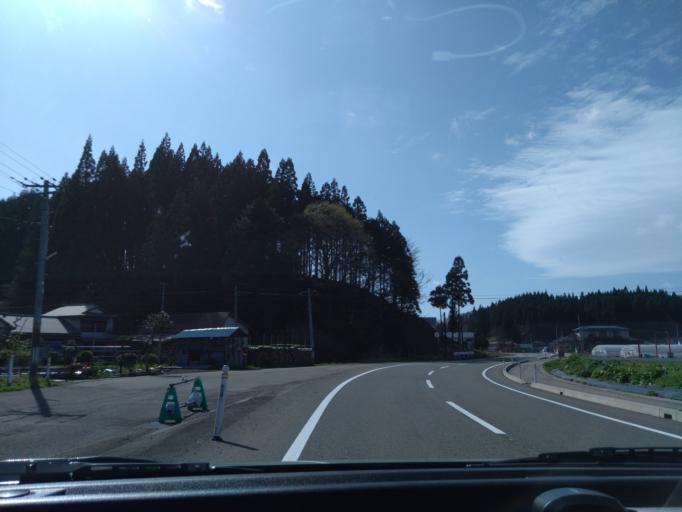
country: JP
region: Akita
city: Akita
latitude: 39.7132
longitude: 140.1999
